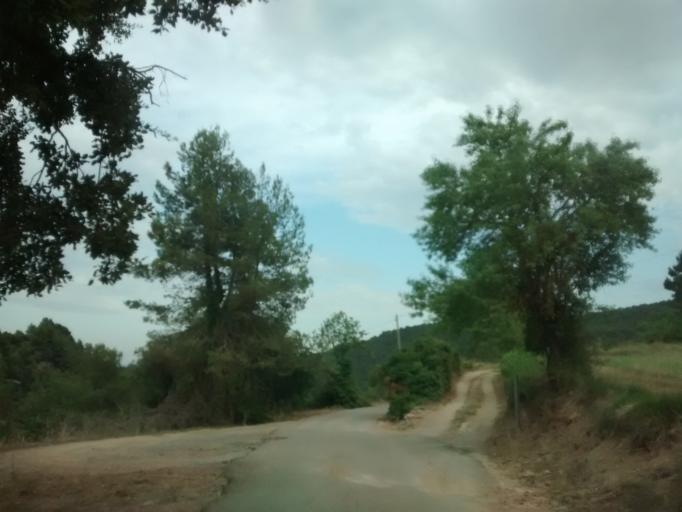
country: ES
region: Catalonia
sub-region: Provincia de Barcelona
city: Fonollosa
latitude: 41.7643
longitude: 1.6891
